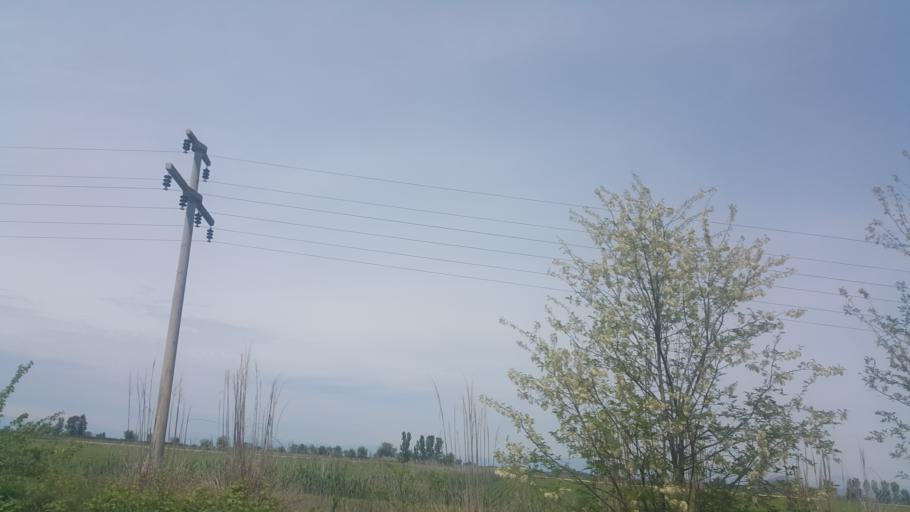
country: TR
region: Osmaniye
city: Toprakkale
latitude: 37.0737
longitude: 36.0484
